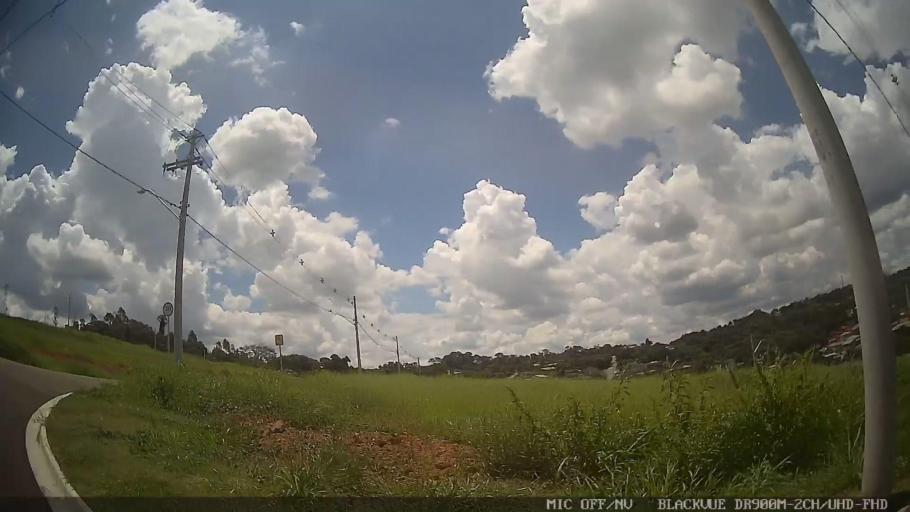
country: BR
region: Sao Paulo
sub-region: Atibaia
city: Atibaia
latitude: -23.1252
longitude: -46.6024
